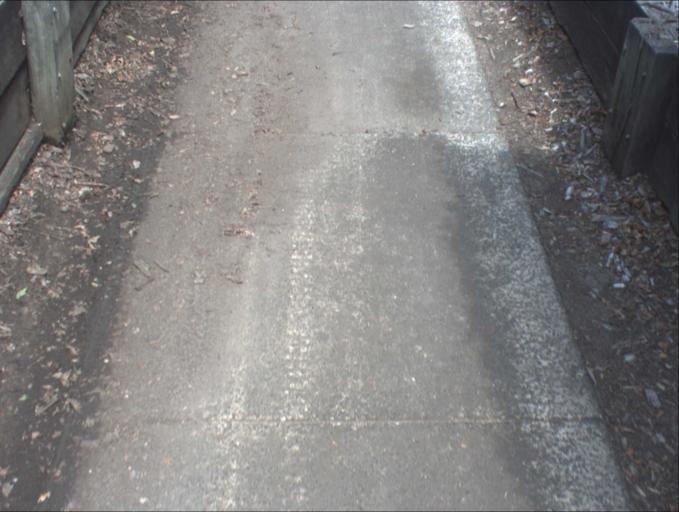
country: AU
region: Queensland
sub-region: Logan
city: Windaroo
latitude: -27.7487
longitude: 153.1956
